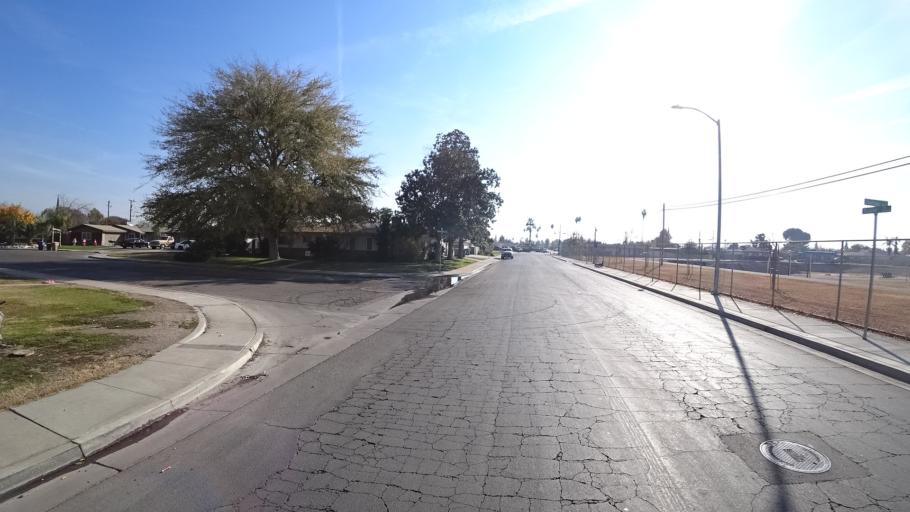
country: US
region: California
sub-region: Kern County
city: Bakersfield
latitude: 35.3222
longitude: -119.0107
